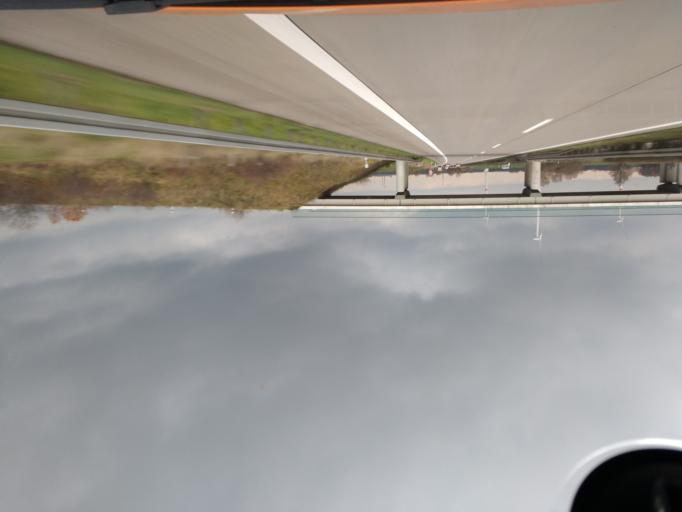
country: DE
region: Brandenburg
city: Heiligengrabe
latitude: 53.1801
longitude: 12.3013
